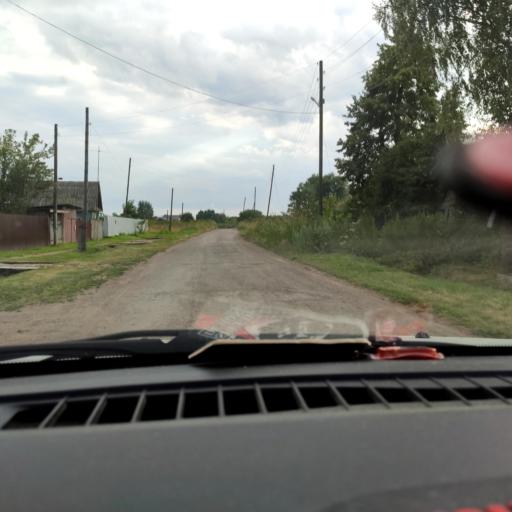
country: RU
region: Perm
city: Kultayevo
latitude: 57.8585
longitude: 55.9739
